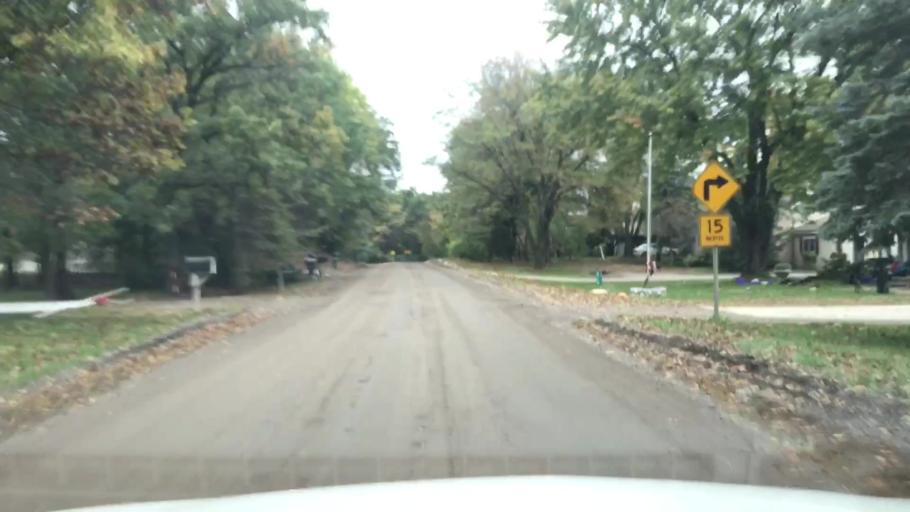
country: US
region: Michigan
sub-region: Oakland County
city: Rochester
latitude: 42.7458
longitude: -83.1214
